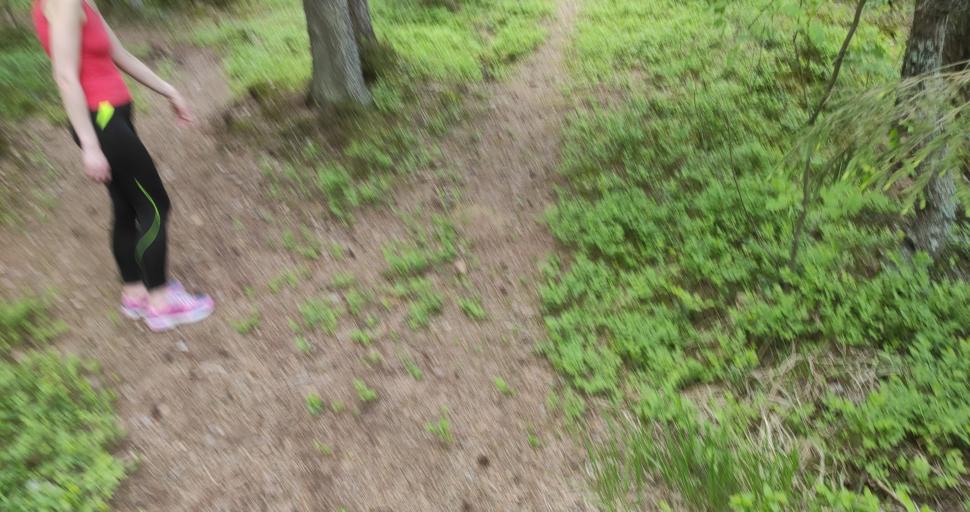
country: LV
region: Talsu Rajons
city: Stende
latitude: 57.1188
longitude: 22.2824
